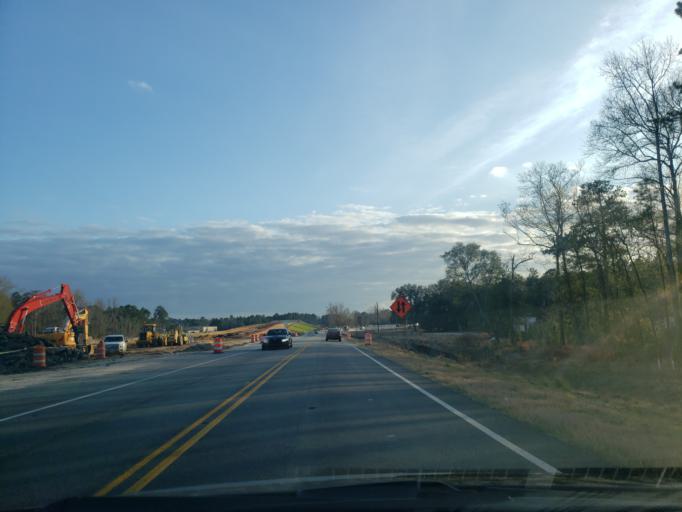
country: US
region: Georgia
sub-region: Chatham County
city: Bloomingdale
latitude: 32.1409
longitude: -81.3087
